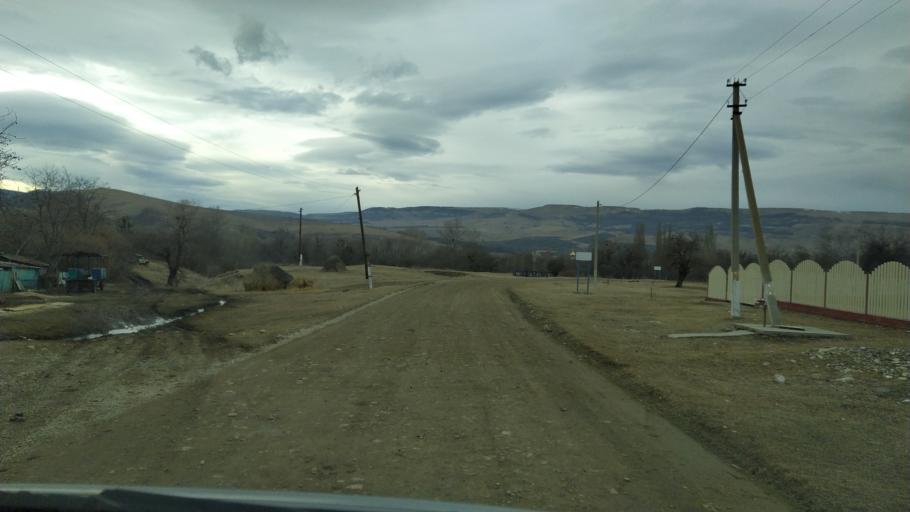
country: RU
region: Krasnodarskiy
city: Peredovaya
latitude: 44.0844
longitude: 41.3654
